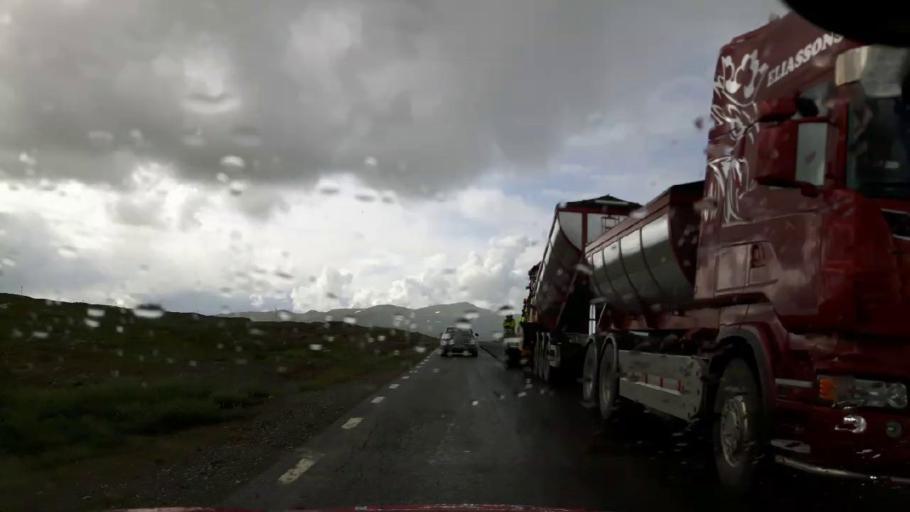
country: NO
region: Nordland
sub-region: Hattfjelldal
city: Hattfjelldal
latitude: 65.0937
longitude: 14.4643
